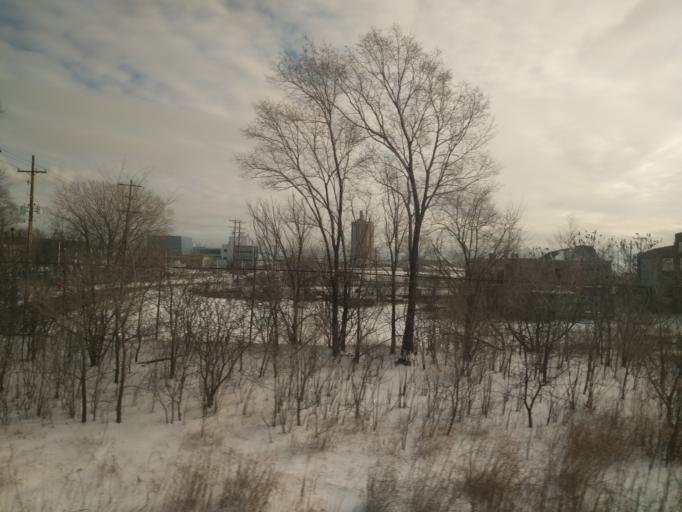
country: US
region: Wisconsin
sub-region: Milwaukee County
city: Milwaukee
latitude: 43.0169
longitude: -87.9090
